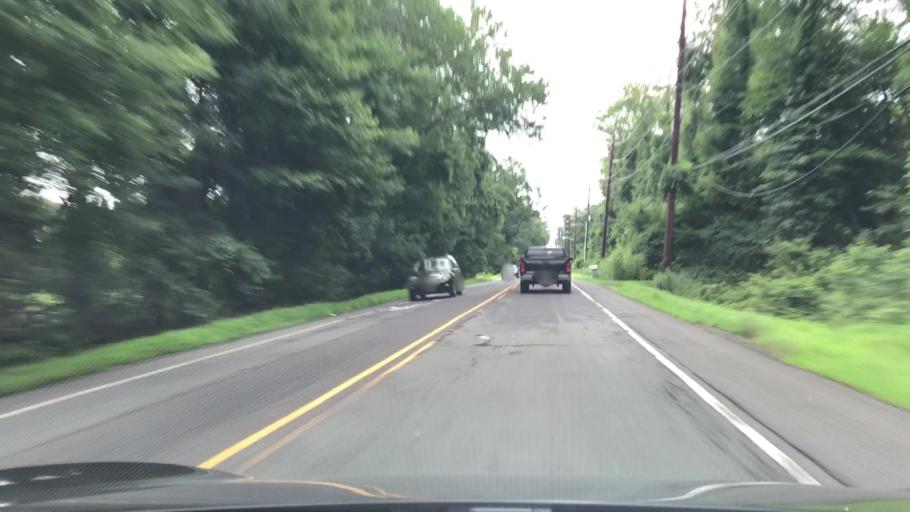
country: US
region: New Jersey
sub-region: Mercer County
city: Lawrenceville
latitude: 40.2965
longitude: -74.7048
